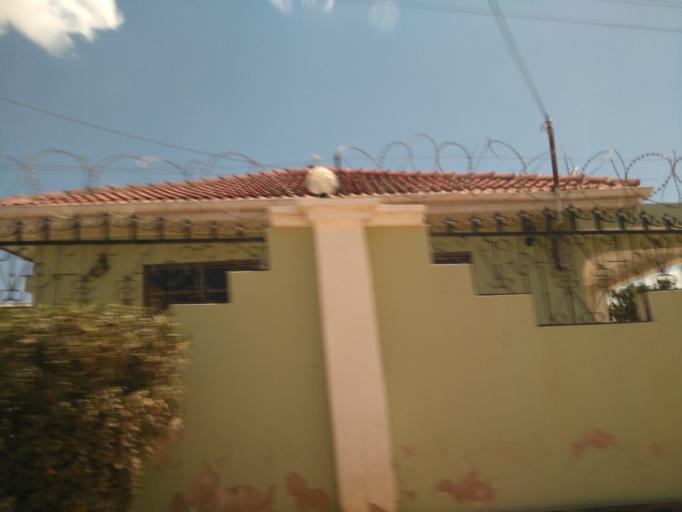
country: TZ
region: Dodoma
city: Kisasa
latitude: -6.1691
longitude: 35.7717
